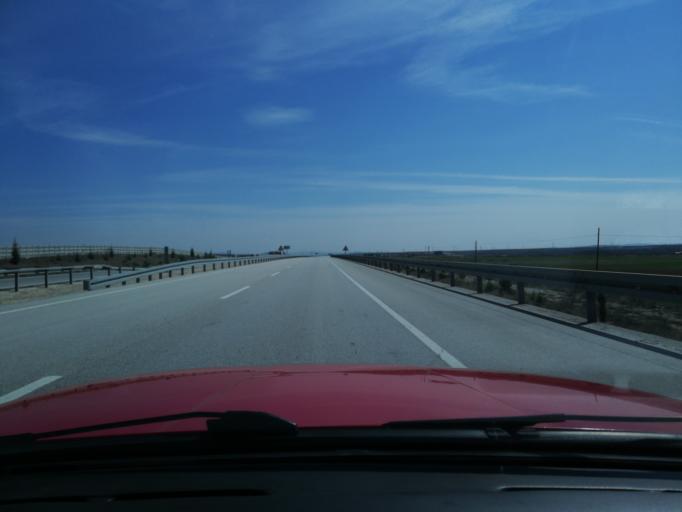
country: TR
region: Kuetahya
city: Altintas
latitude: 39.0874
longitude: 30.1926
